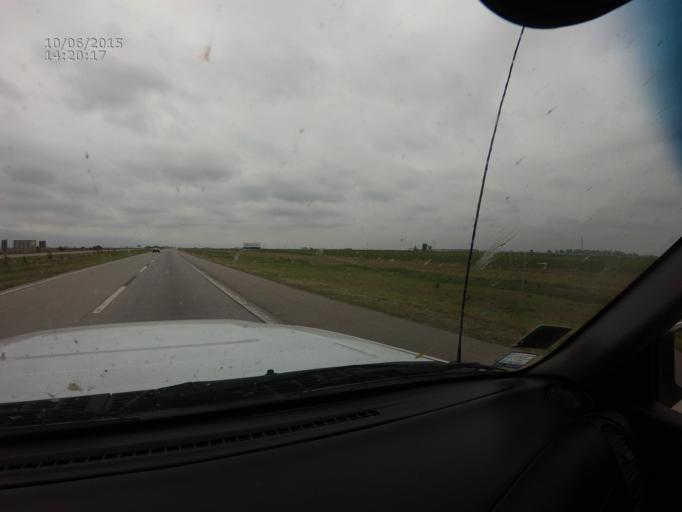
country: AR
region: Cordoba
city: Villa Maria
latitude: -32.3459
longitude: -63.2501
